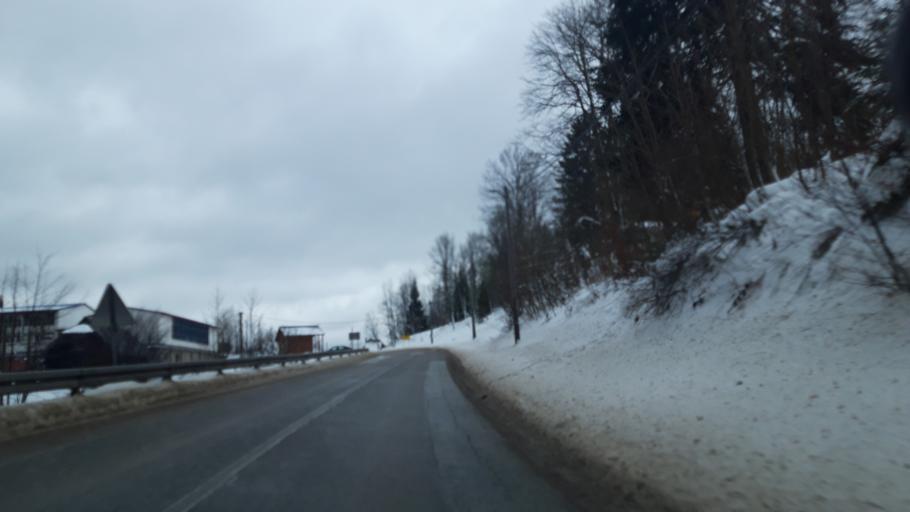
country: BA
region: Republika Srpska
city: Han Pijesak
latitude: 44.0860
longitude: 18.9536
